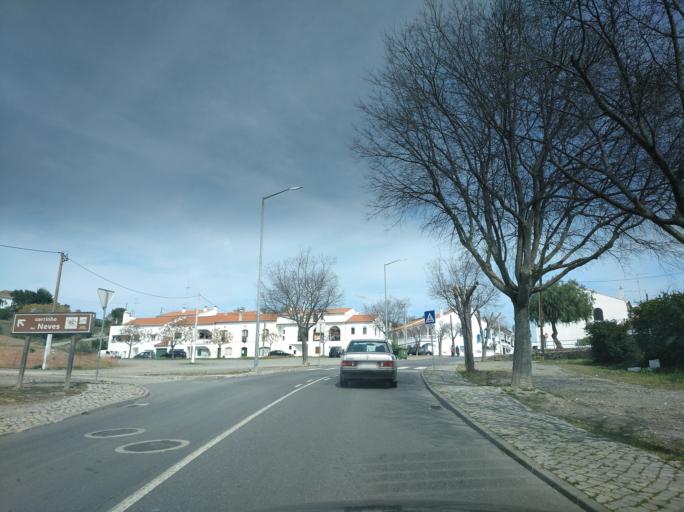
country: PT
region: Beja
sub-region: Mertola
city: Mertola
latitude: 37.6424
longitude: -7.6632
